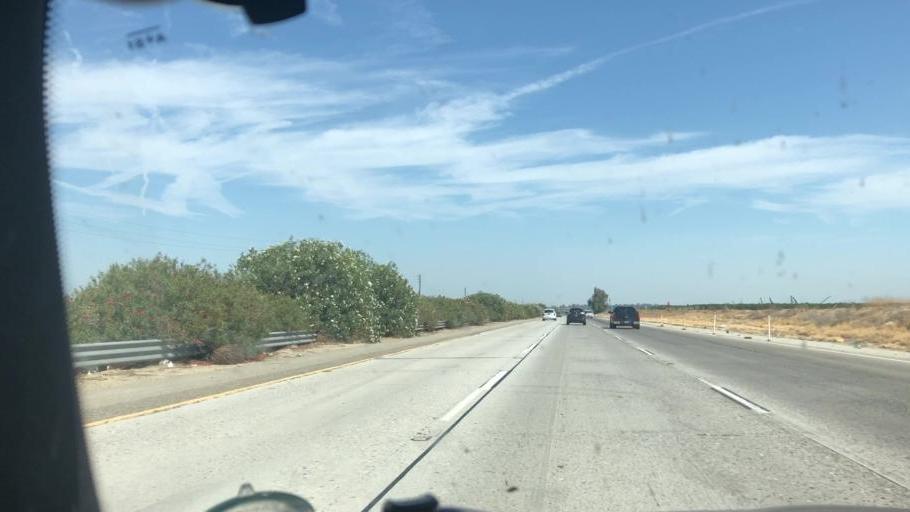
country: US
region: California
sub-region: Kern County
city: Weedpatch
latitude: 35.1273
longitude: -118.9898
